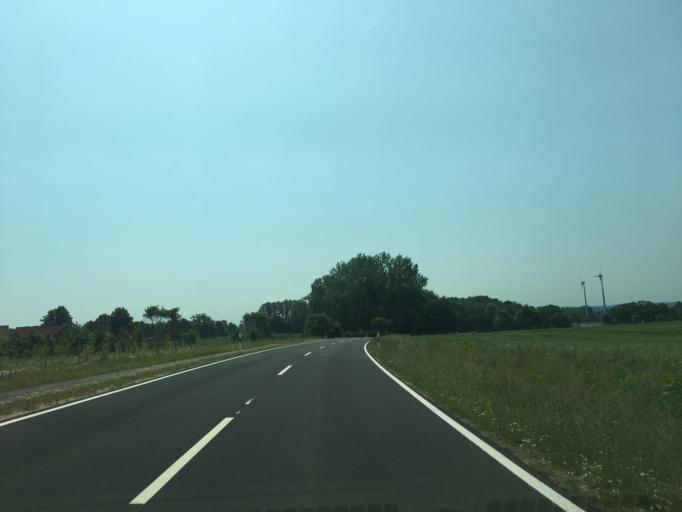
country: DE
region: North Rhine-Westphalia
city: Olfen
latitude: 51.7360
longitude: 7.4023
